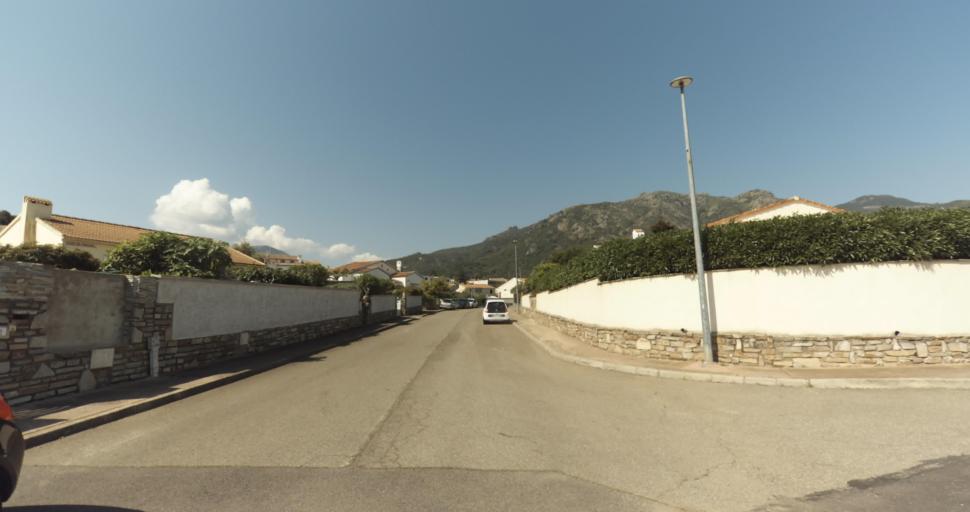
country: FR
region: Corsica
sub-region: Departement de la Haute-Corse
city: Biguglia
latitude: 42.6275
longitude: 9.4339
